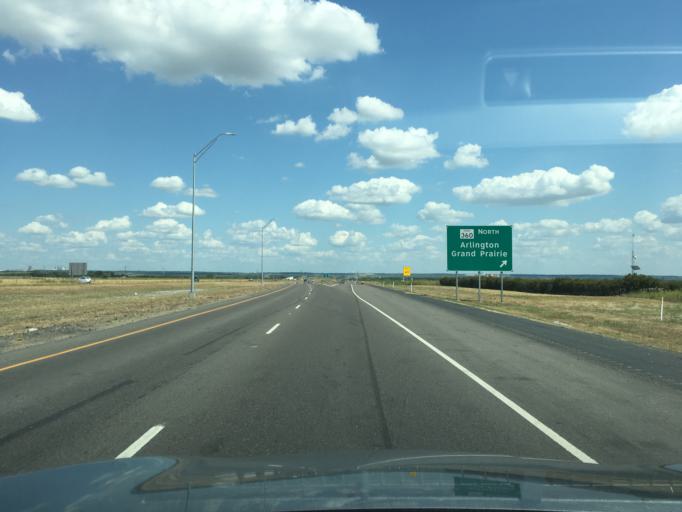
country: US
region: Texas
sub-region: Tarrant County
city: Mansfield
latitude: 32.5288
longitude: -97.0948
